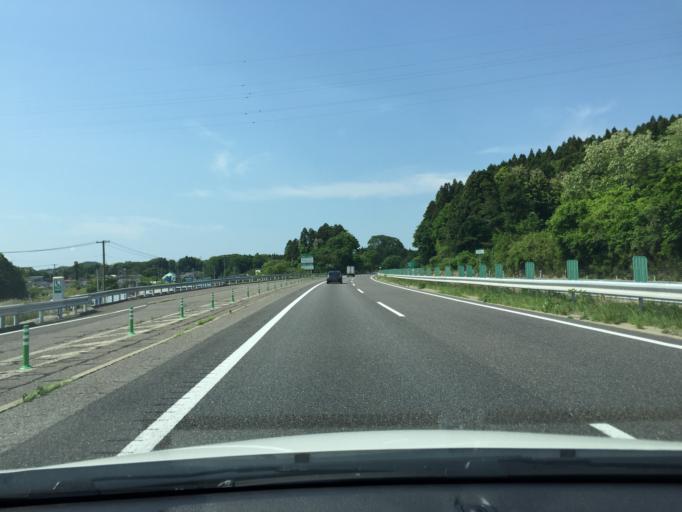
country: JP
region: Fukushima
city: Sukagawa
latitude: 37.1881
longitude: 140.2925
